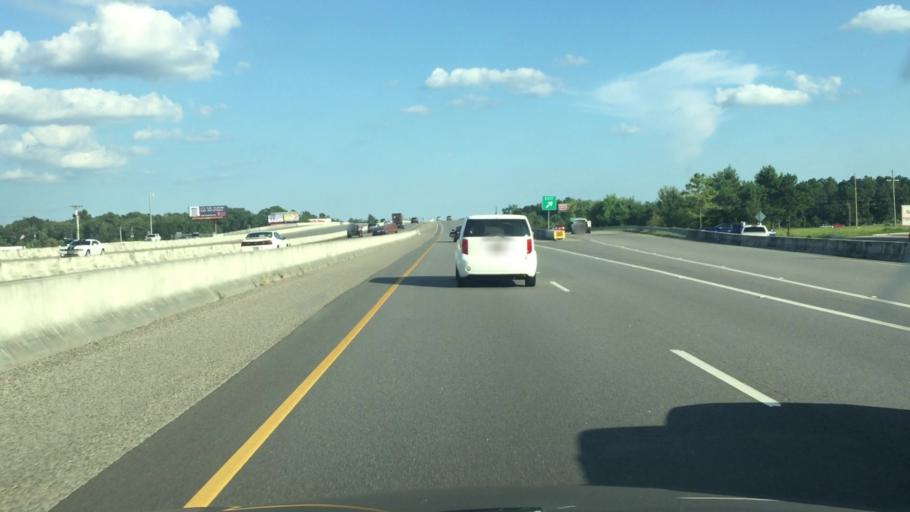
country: US
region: South Carolina
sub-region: Horry County
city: Forestbrook
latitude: 33.7355
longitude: -78.9475
